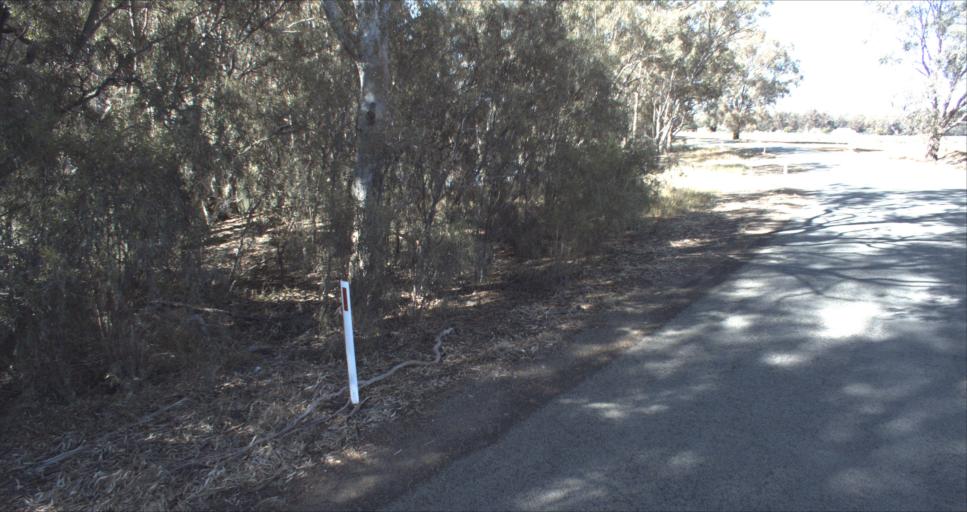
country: AU
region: New South Wales
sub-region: Leeton
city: Leeton
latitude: -34.6098
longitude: 146.2604
